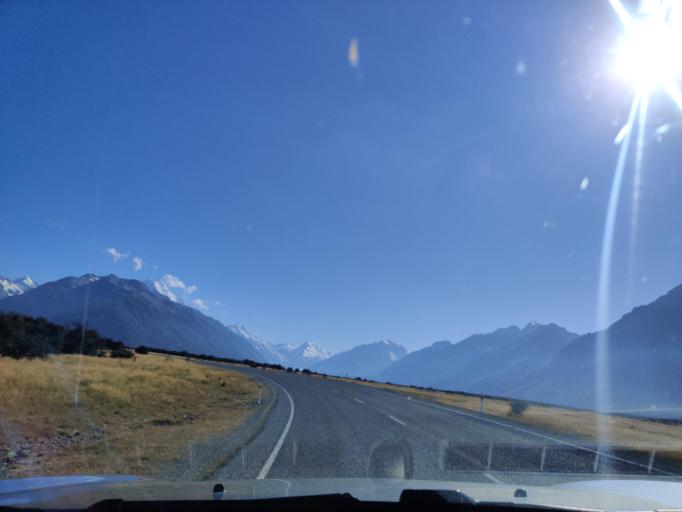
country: NZ
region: Canterbury
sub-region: Timaru District
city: Pleasant Point
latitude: -43.7830
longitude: 170.1235
